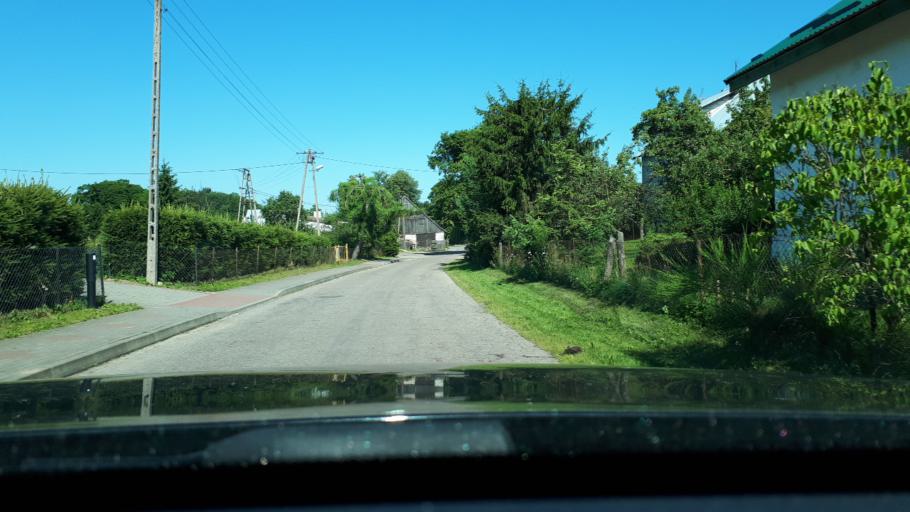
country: PL
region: Warmian-Masurian Voivodeship
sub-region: Powiat ostrodzki
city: Gierzwald
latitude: 53.6466
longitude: 20.1045
